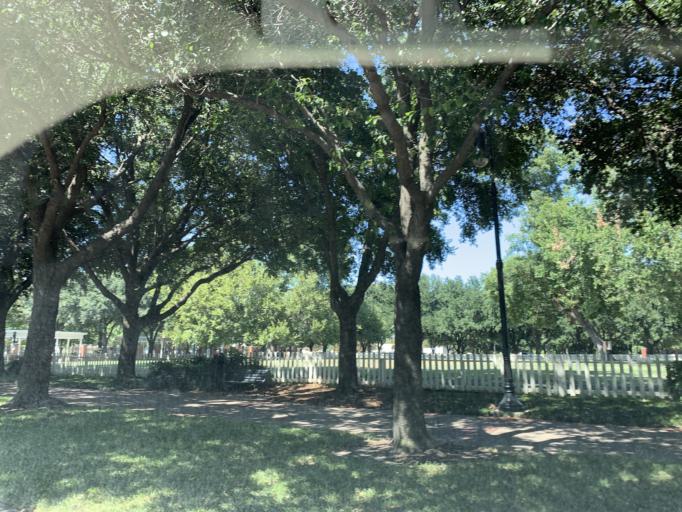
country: US
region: Texas
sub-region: Dallas County
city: Dallas
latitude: 32.7891
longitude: -96.7863
